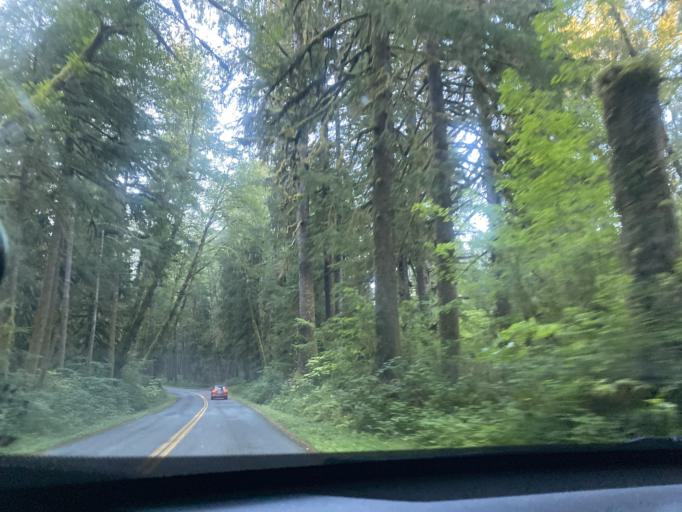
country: US
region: Washington
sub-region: Clallam County
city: Forks
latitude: 47.8157
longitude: -124.1090
